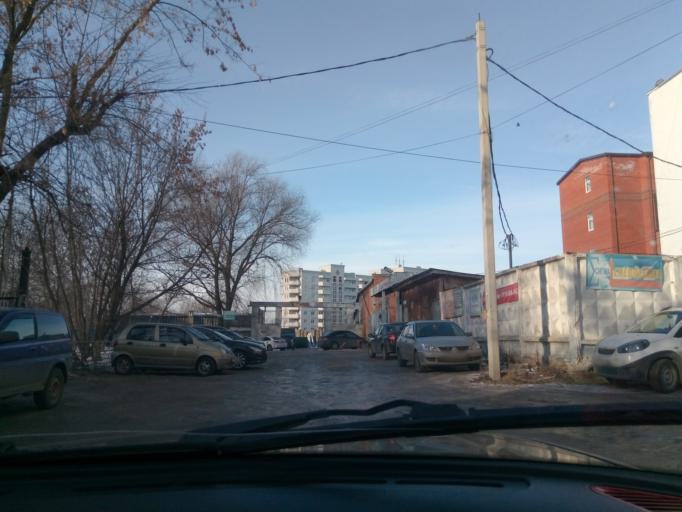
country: RU
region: Tula
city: Mendeleyevskiy
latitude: 54.1724
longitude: 37.5724
